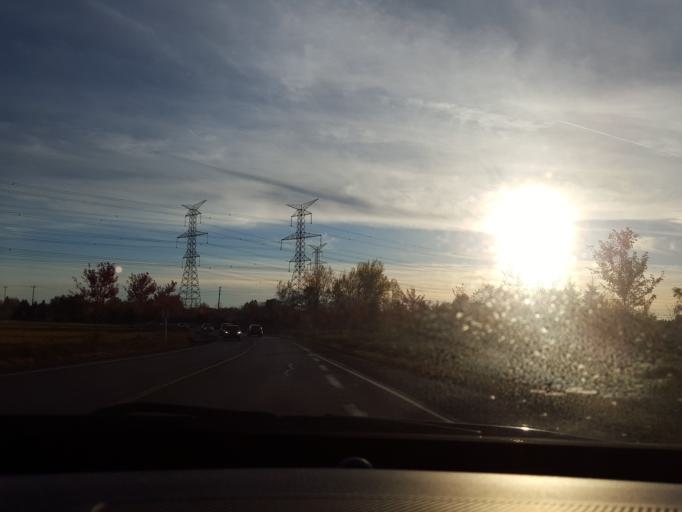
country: CA
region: Ontario
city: Markham
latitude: 43.8507
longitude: -79.2256
